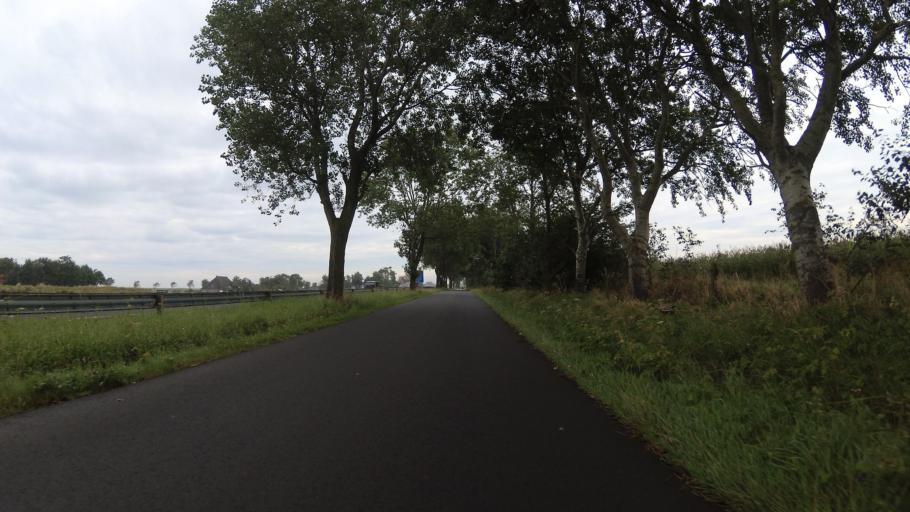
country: NL
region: North Holland
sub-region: Gemeente Hollands Kroon
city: Den Oever
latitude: 52.8947
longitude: 4.9213
